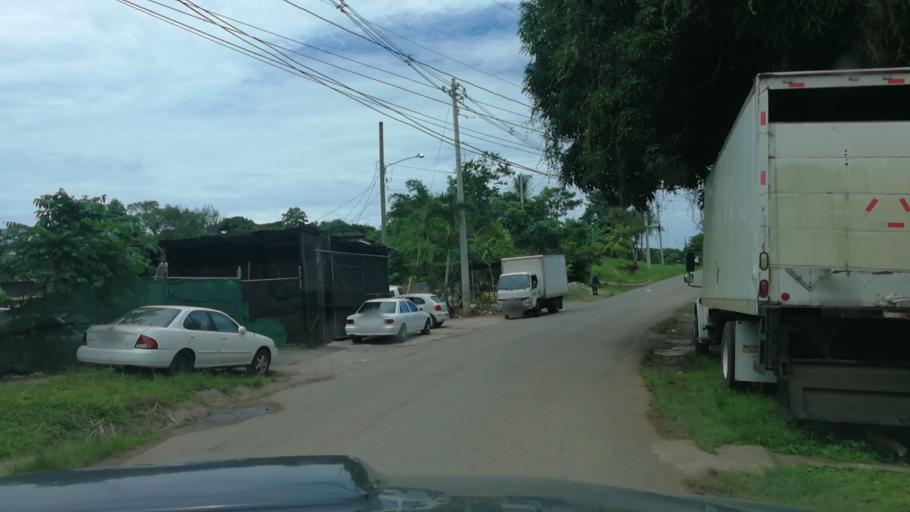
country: PA
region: Panama
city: San Miguelito
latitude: 9.0971
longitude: -79.4559
